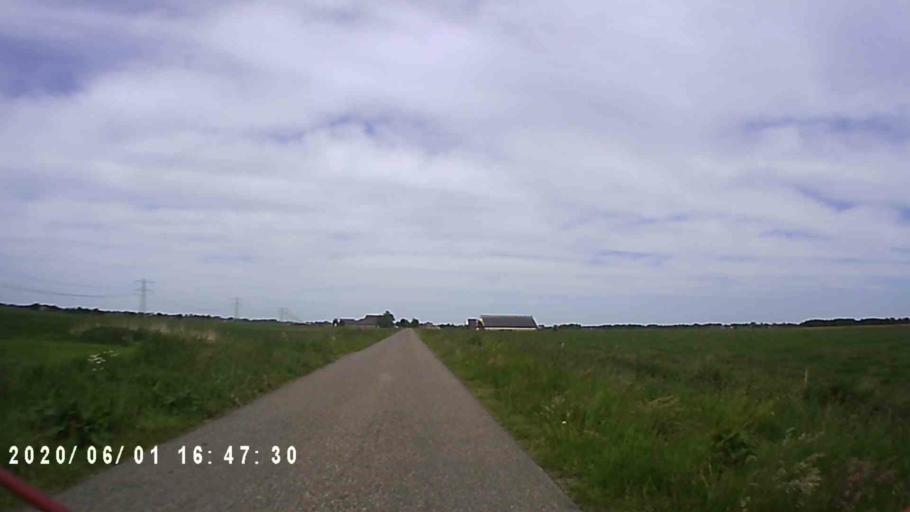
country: NL
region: Friesland
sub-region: Gemeente Tytsjerksteradiel
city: Tytsjerk
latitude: 53.1865
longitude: 5.8966
